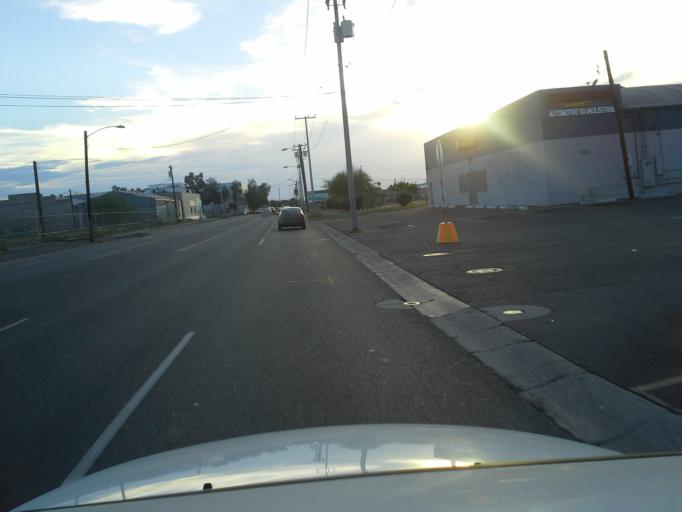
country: US
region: Arizona
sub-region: Maricopa County
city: Phoenix
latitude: 33.4369
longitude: -112.0672
